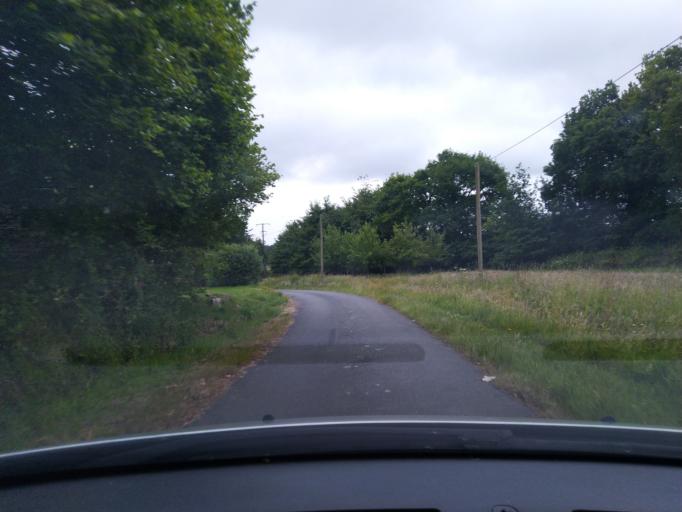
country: FR
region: Brittany
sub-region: Departement des Cotes-d'Armor
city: Begard
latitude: 48.6381
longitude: -3.3270
